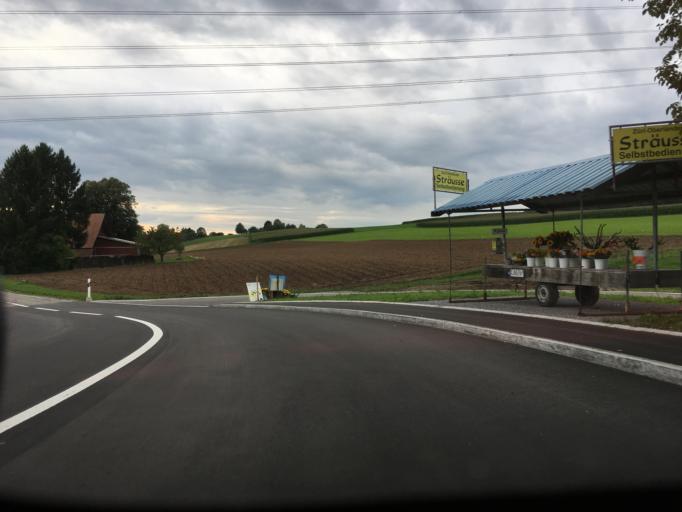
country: CH
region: Zurich
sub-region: Bezirk Uster
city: Gutenswil
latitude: 47.3855
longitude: 8.7096
